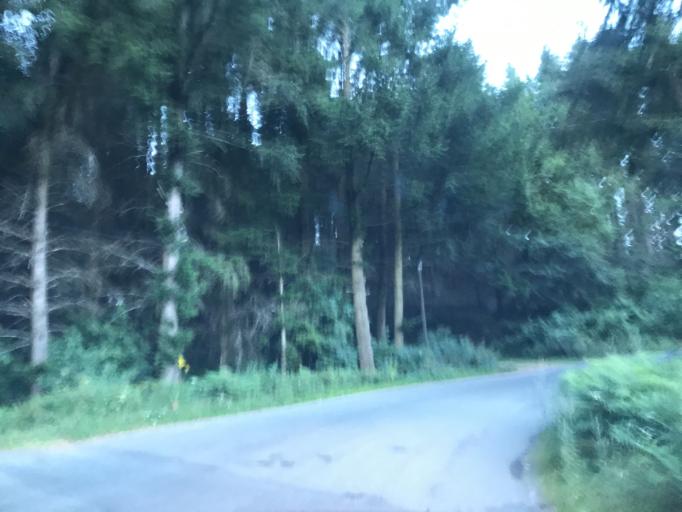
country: FR
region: Rhone-Alpes
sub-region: Departement de la Loire
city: Noiretable
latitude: 45.8115
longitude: 3.7313
